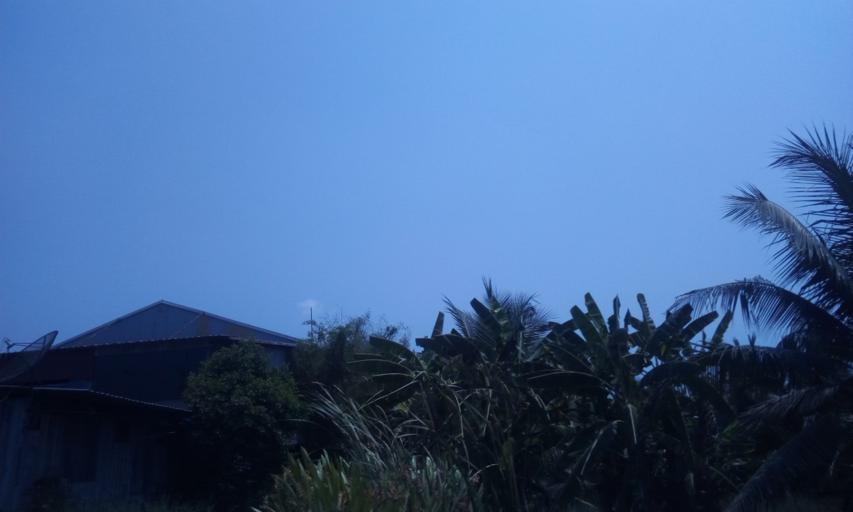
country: TH
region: Chachoengsao
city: Bang Nam Priao
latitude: 13.8658
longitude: 100.9667
